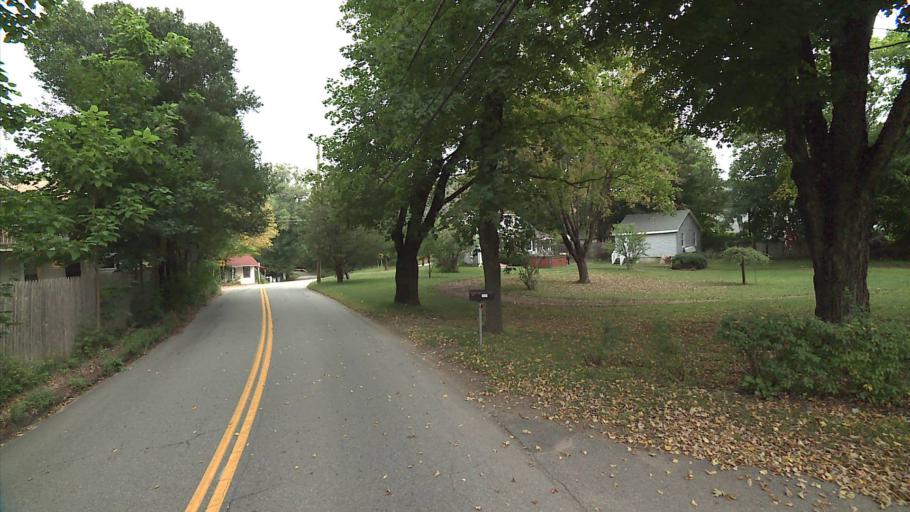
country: US
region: Connecticut
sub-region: Tolland County
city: South Coventry
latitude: 41.7852
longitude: -72.2788
